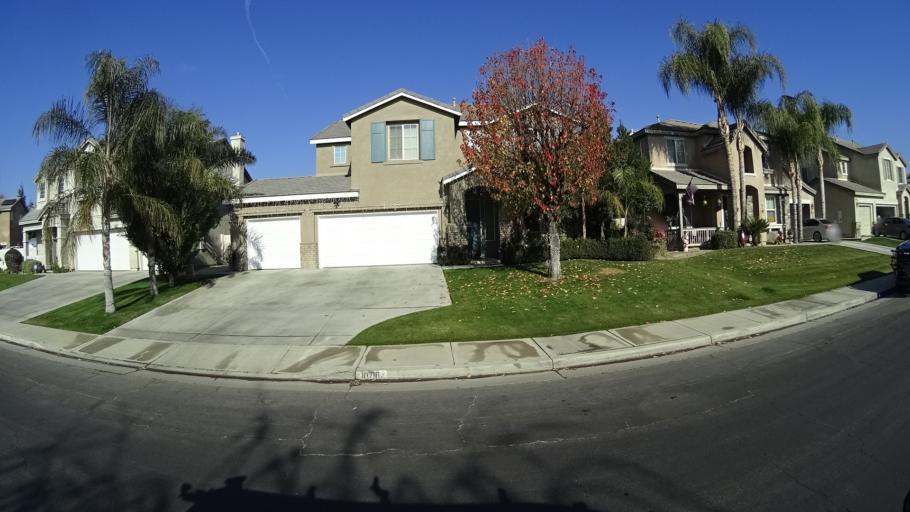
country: US
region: California
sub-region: Kern County
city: Greenacres
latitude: 35.3154
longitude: -119.1218
